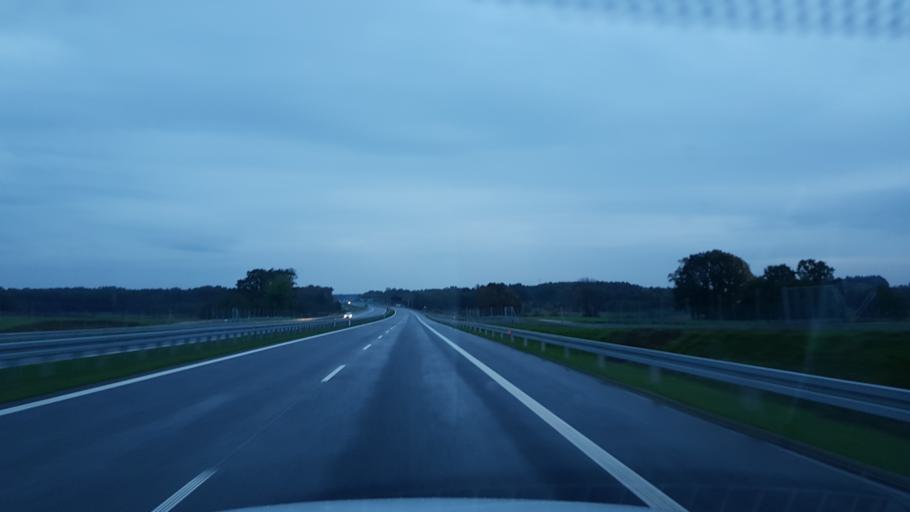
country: PL
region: West Pomeranian Voivodeship
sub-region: Powiat gryficki
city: Brojce
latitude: 53.9258
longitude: 15.3879
